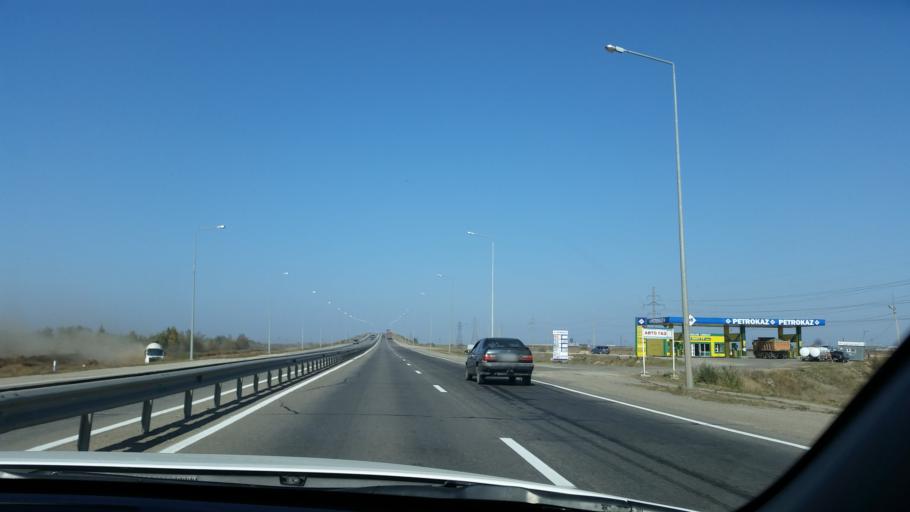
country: KZ
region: Astana Qalasy
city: Astana
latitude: 51.2194
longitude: 71.3207
